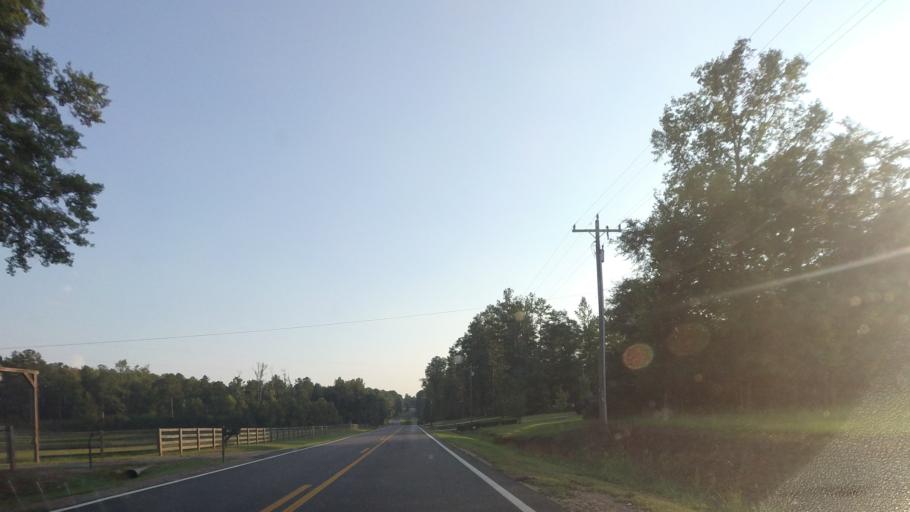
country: US
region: Georgia
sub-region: Bibb County
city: West Point
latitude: 32.9135
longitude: -83.8183
